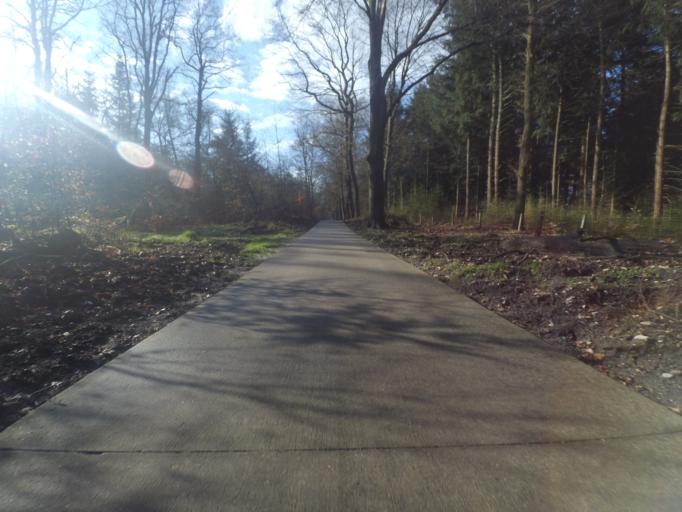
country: NL
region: Gelderland
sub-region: Gemeente Ede
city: Otterlo
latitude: 52.1296
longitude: 5.8636
